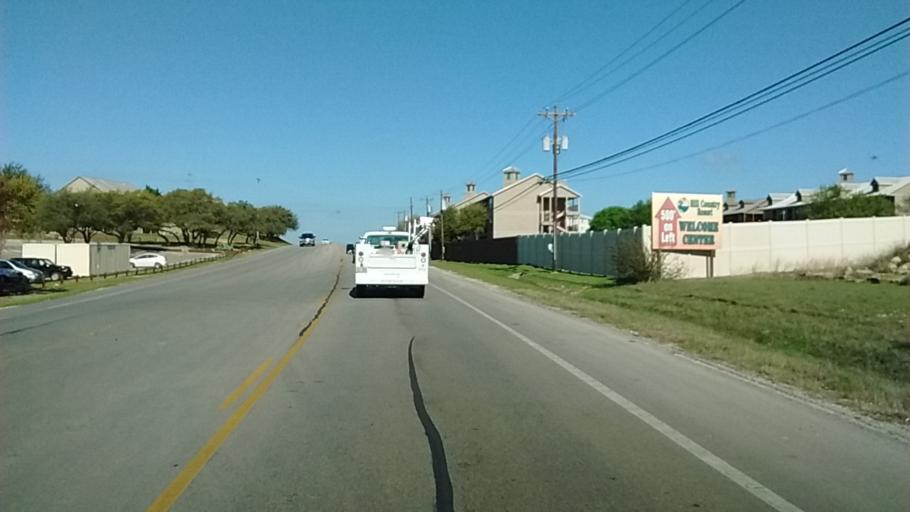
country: US
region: Texas
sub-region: Comal County
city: Canyon Lake
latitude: 29.9084
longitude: -98.2085
